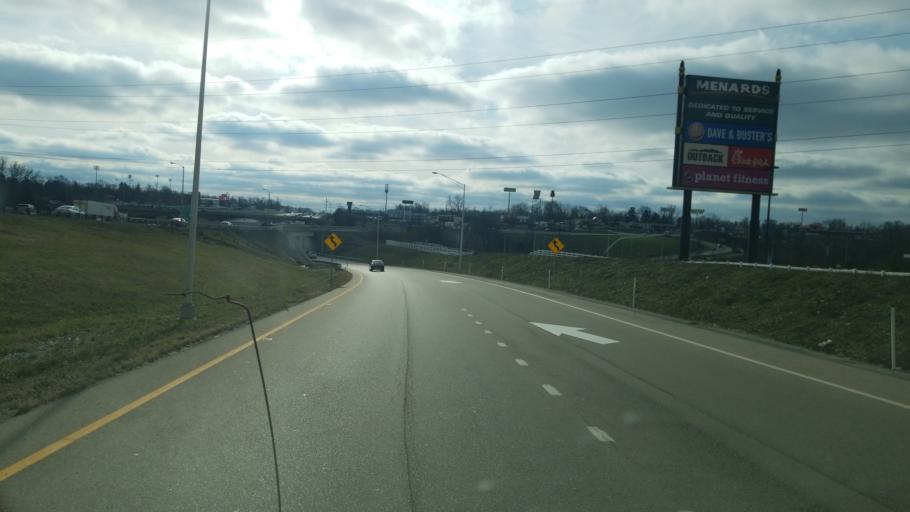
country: US
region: Kentucky
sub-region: Boone County
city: Florence
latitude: 38.9879
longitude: -84.6437
